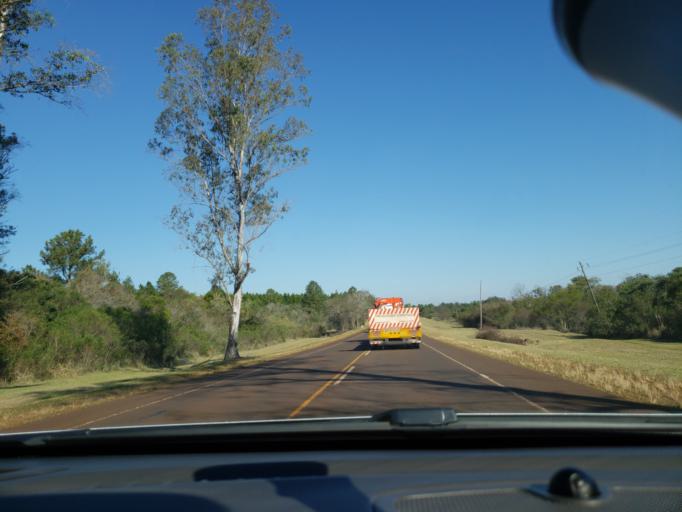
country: AR
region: Misiones
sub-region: Departamento de Apostoles
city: San Jose
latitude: -27.8188
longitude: -55.7696
